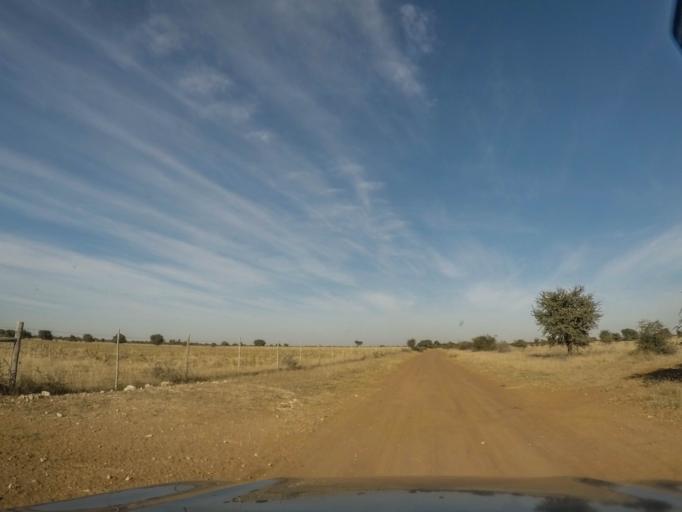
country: BW
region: South East
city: Janeng
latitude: -25.5668
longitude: 25.3088
